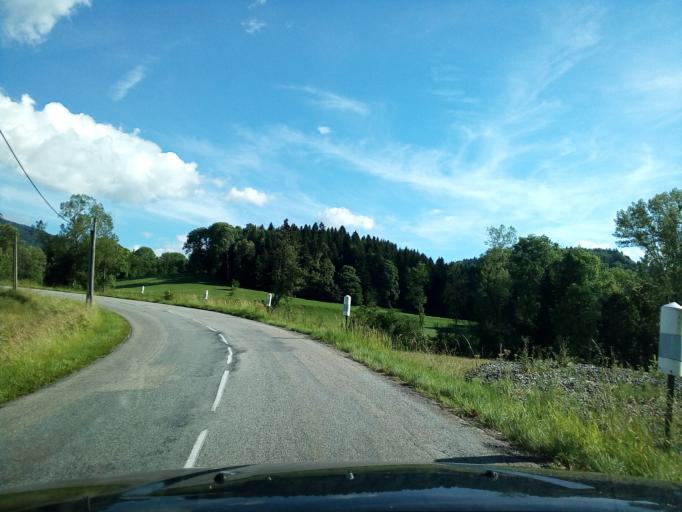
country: FR
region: Rhone-Alpes
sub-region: Departement de la Savoie
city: La Bridoire
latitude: 45.5189
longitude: 5.7667
